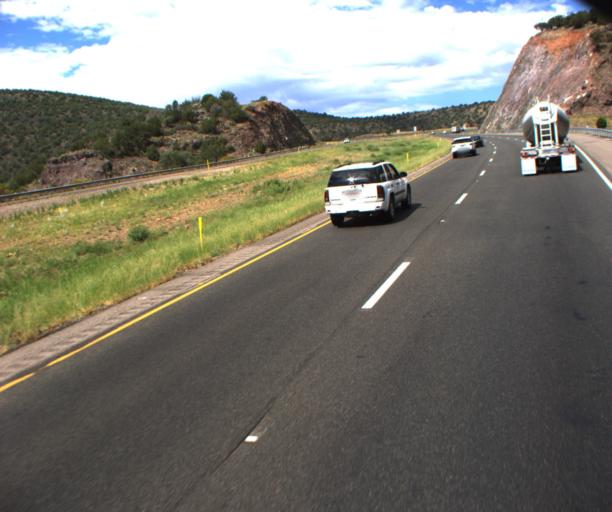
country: US
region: Arizona
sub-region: Yavapai County
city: Camp Verde
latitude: 34.5311
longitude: -111.9448
